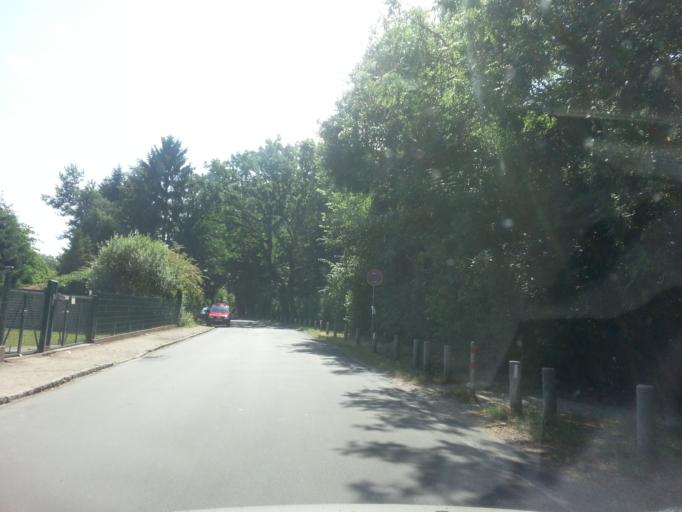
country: DE
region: Rheinland-Pfalz
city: Worms
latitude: 49.6218
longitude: 8.3713
